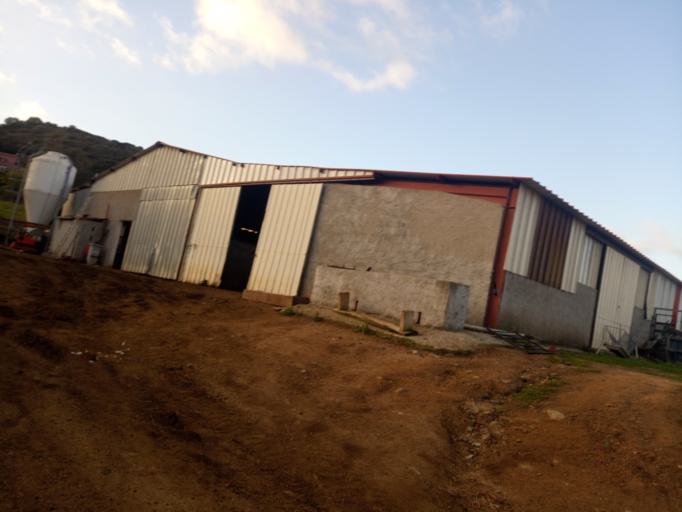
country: FR
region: Corsica
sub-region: Departement de la Corse-du-Sud
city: Appietto
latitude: 42.0717
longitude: 8.7267
